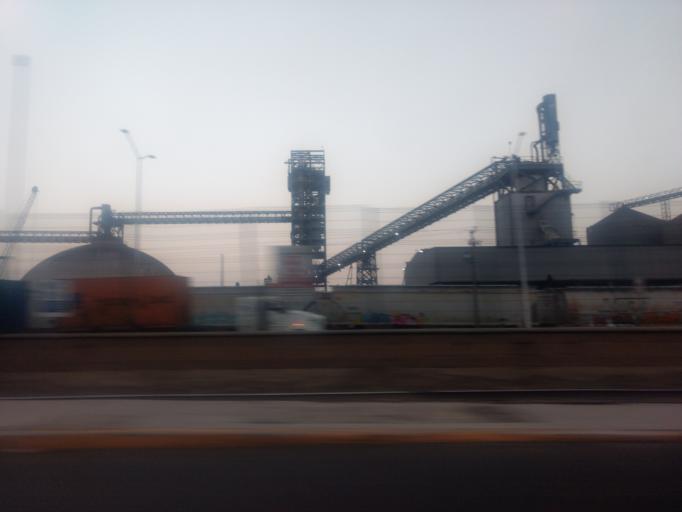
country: MX
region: Colima
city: Tapeixtles
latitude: 19.0629
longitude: -104.2900
